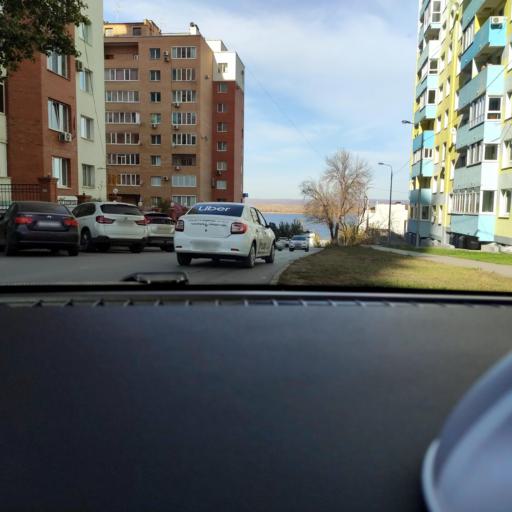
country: RU
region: Samara
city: Samara
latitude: 53.2249
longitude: 50.1518
